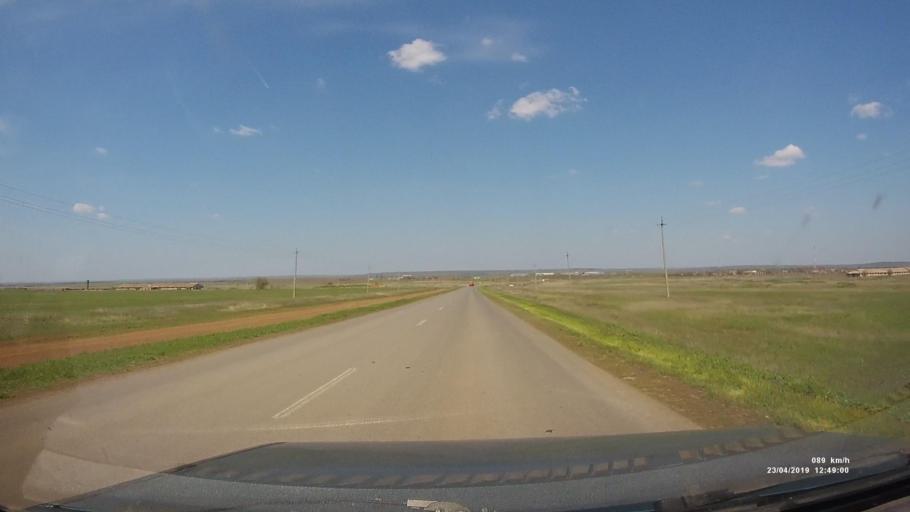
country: RU
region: Kalmykiya
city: Yashalta
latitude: 46.5318
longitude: 42.6389
